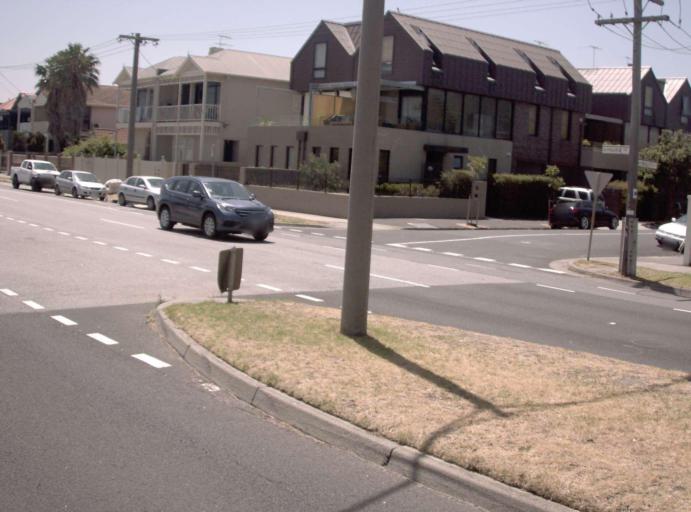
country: AU
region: Victoria
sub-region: Port Phillip
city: Elwood
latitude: -37.8773
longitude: 144.9770
